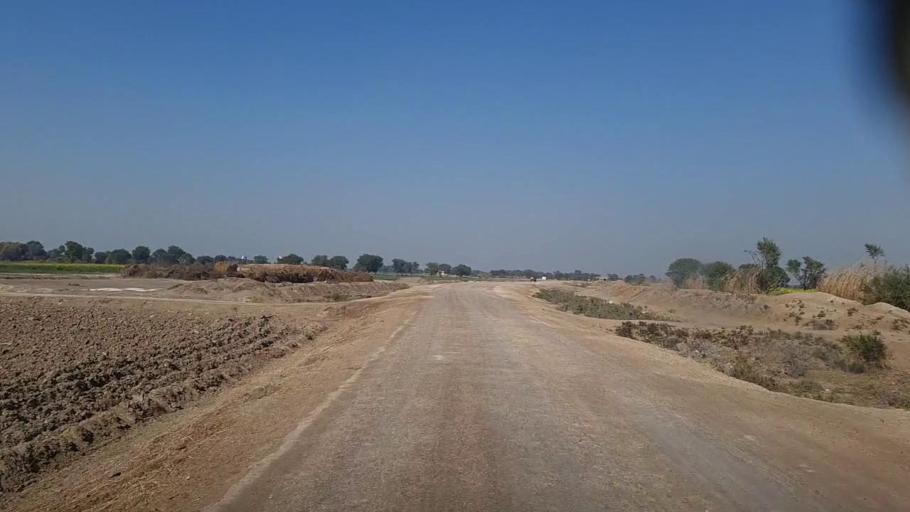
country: PK
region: Sindh
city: Khairpur
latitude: 27.9878
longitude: 69.8483
